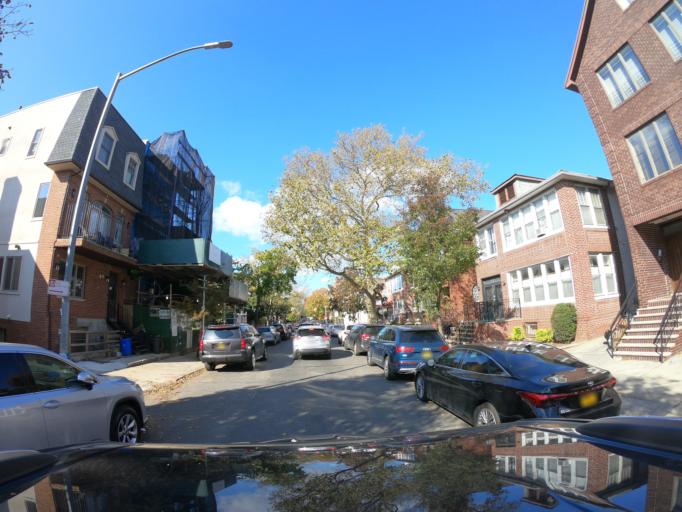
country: US
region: New York
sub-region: Kings County
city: Bensonhurst
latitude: 40.6269
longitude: -73.9846
